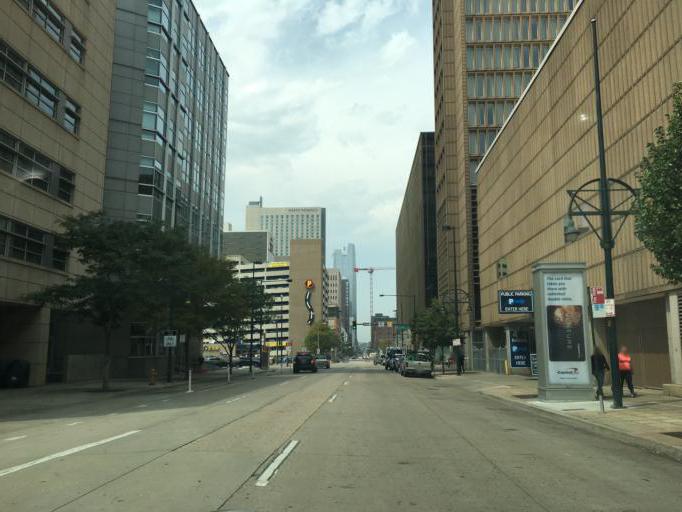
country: US
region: Colorado
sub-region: Denver County
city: Denver
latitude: 39.7411
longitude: -104.9892
